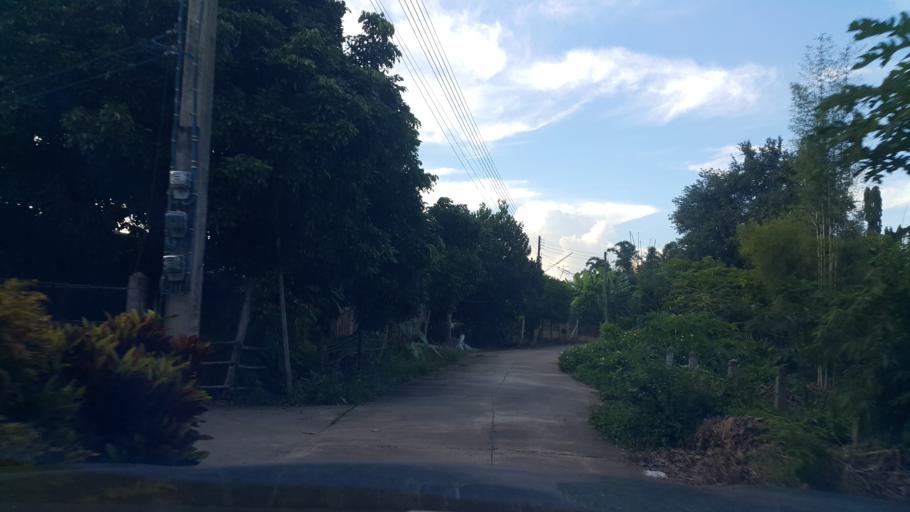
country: TH
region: Chiang Mai
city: Mae Taeng
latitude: 19.1616
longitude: 99.0086
